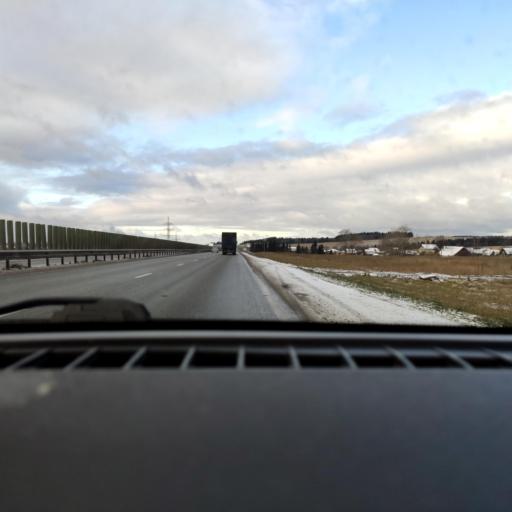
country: RU
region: Perm
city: Froly
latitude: 57.9340
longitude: 56.2532
